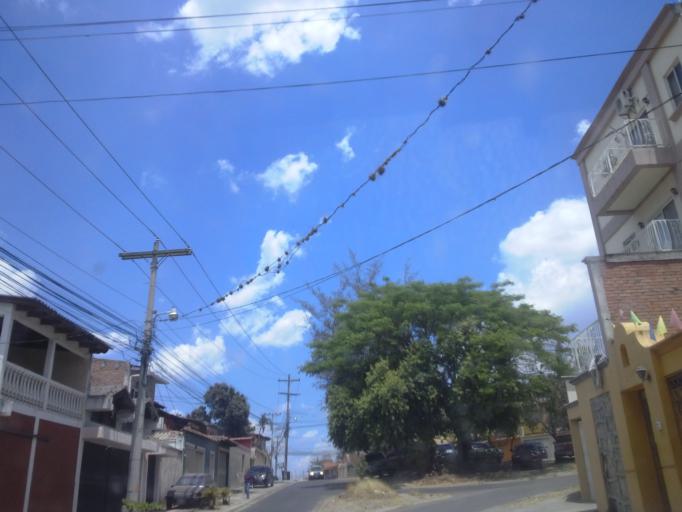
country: HN
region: Francisco Morazan
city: Yaguacire
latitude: 14.0490
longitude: -87.2325
